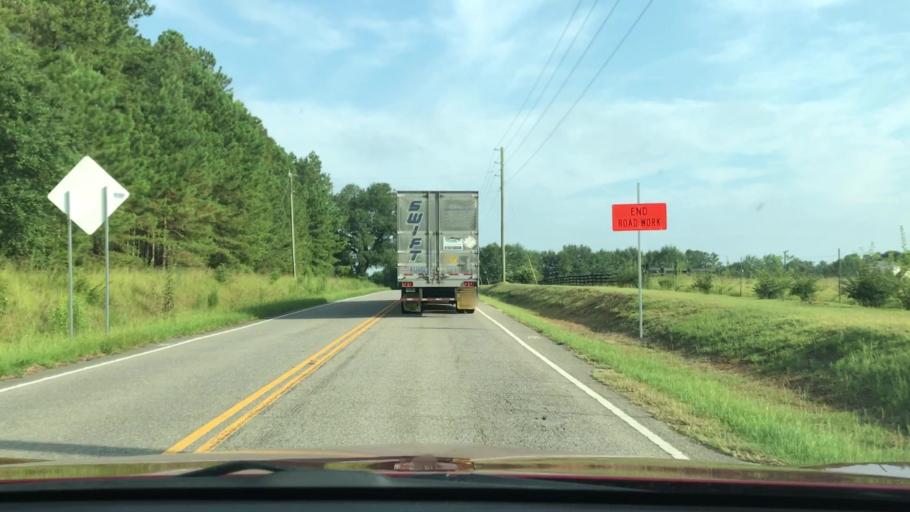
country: US
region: South Carolina
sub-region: Barnwell County
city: Blackville
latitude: 33.6052
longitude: -81.2665
